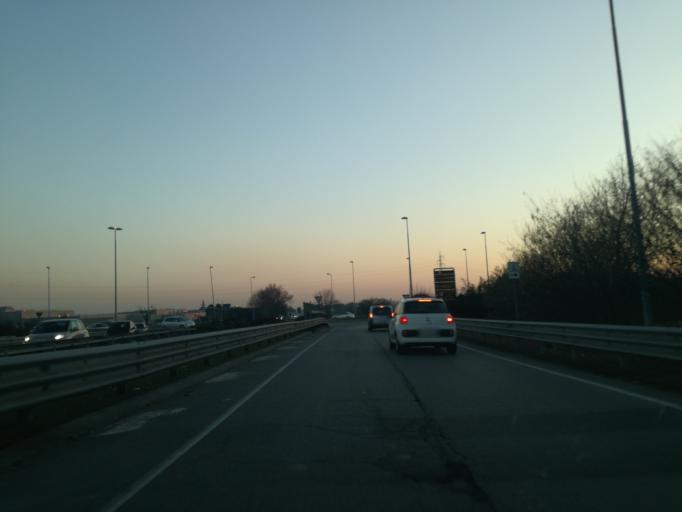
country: IT
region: Lombardy
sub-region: Provincia di Lecco
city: Cernusco Lombardone
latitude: 45.6893
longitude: 9.4004
